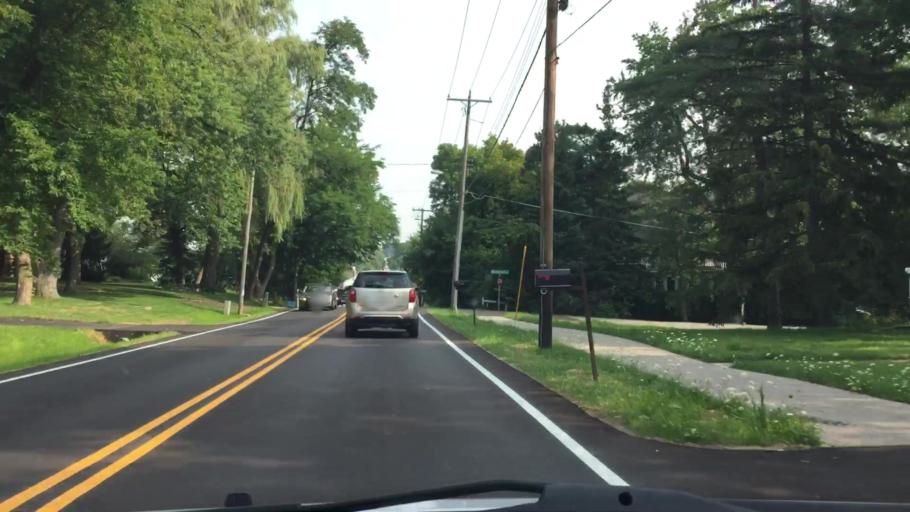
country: US
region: Wisconsin
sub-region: Waukesha County
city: Brookfield
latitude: 43.0693
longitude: -88.1459
